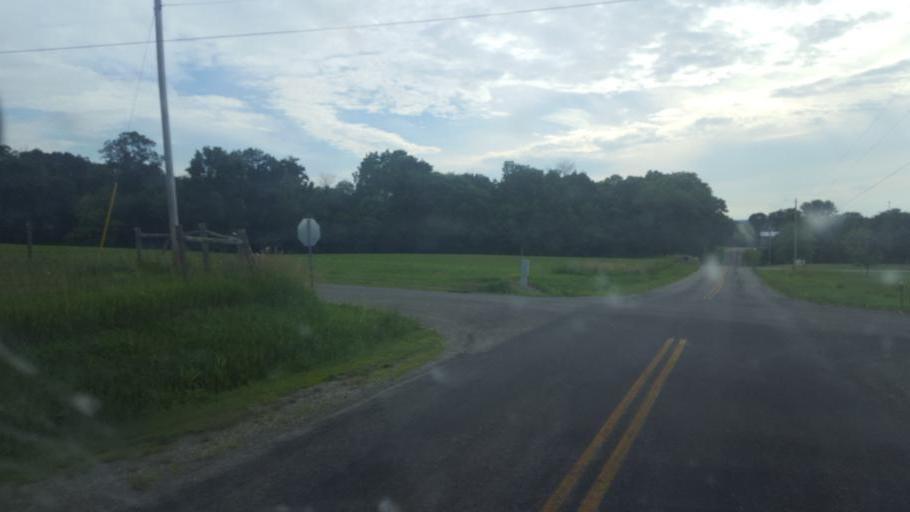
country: US
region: Ohio
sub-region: Ashland County
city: Loudonville
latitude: 40.7715
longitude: -82.1981
